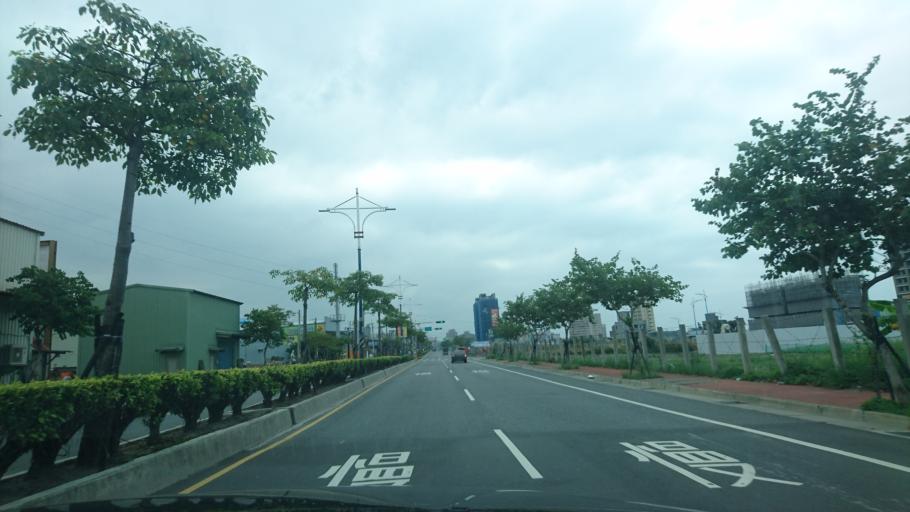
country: TW
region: Taipei
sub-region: Taipei
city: Banqiao
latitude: 25.1545
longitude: 121.4141
